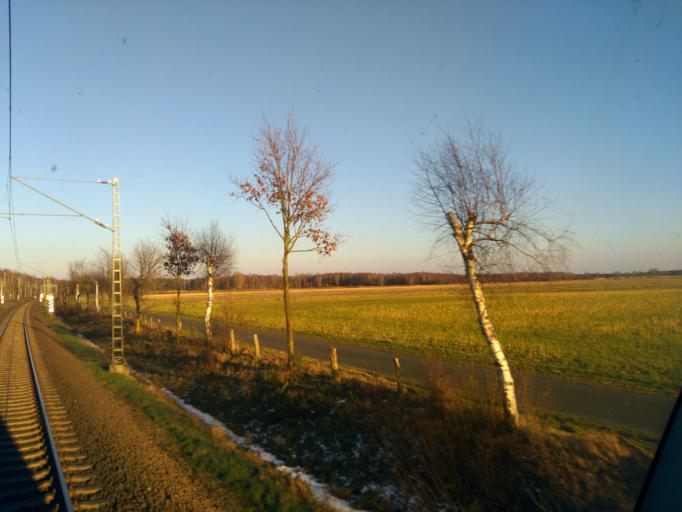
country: DE
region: Lower Saxony
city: Lauenbruck
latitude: 53.1873
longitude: 9.5292
